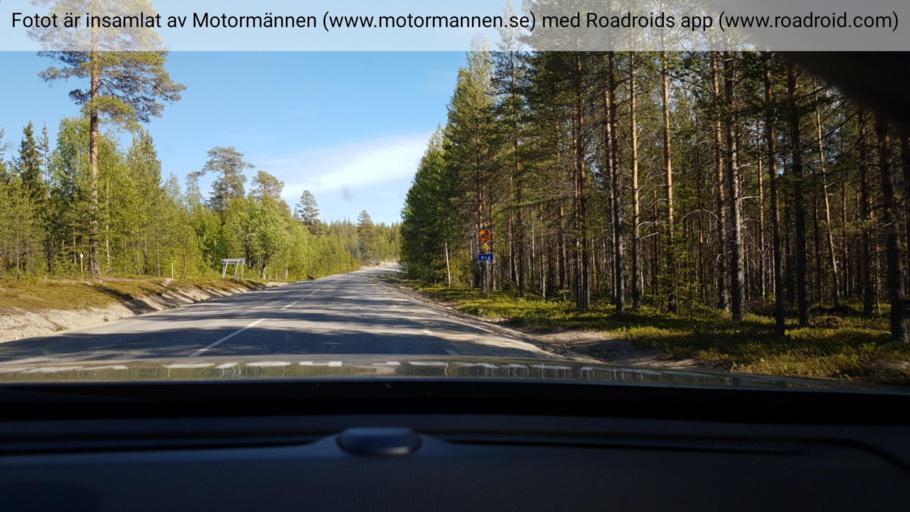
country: SE
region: Vaesterbotten
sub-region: Norsjo Kommun
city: Norsjoe
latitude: 64.7110
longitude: 19.1491
